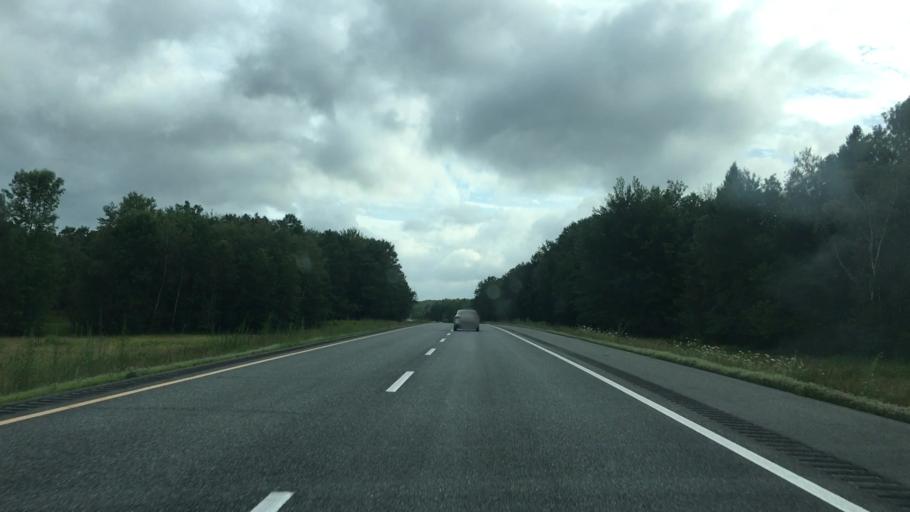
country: US
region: Maine
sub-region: Kennebec County
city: Clinton
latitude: 44.6492
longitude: -69.5178
